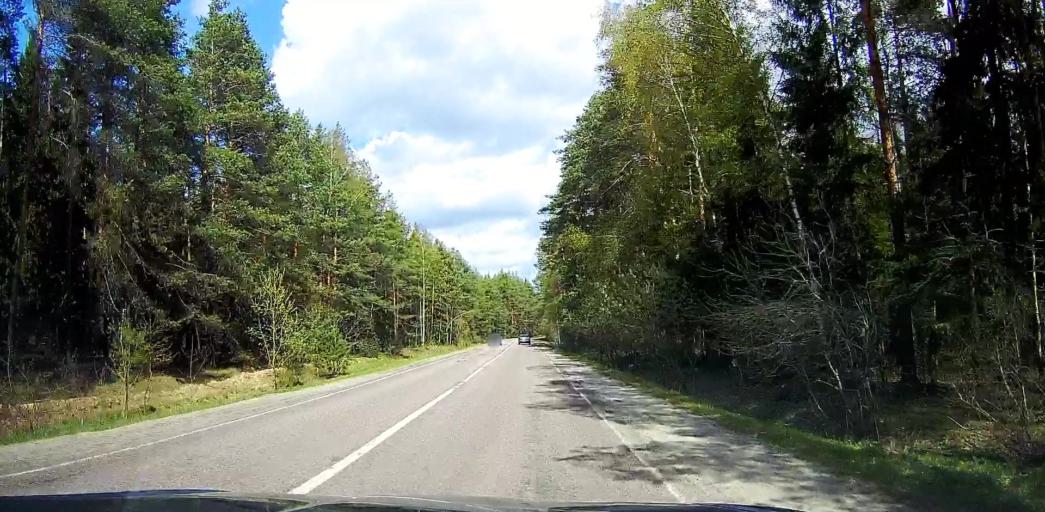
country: RU
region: Moskovskaya
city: Davydovo
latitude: 55.5638
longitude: 38.8151
